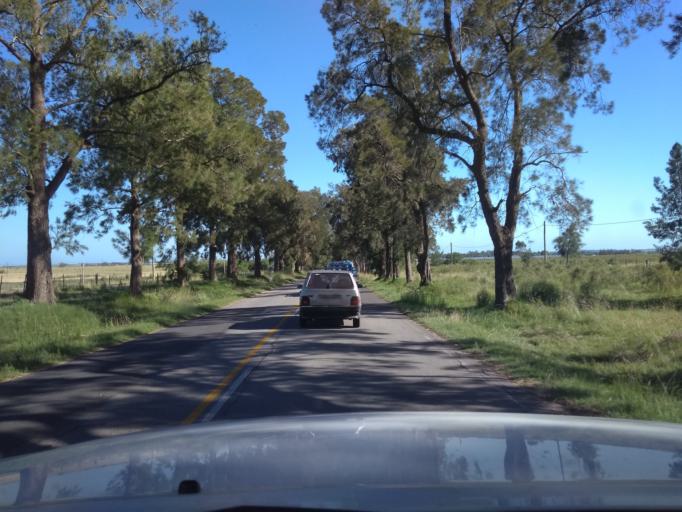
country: UY
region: Canelones
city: San Bautista
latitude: -34.3957
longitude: -55.9596
